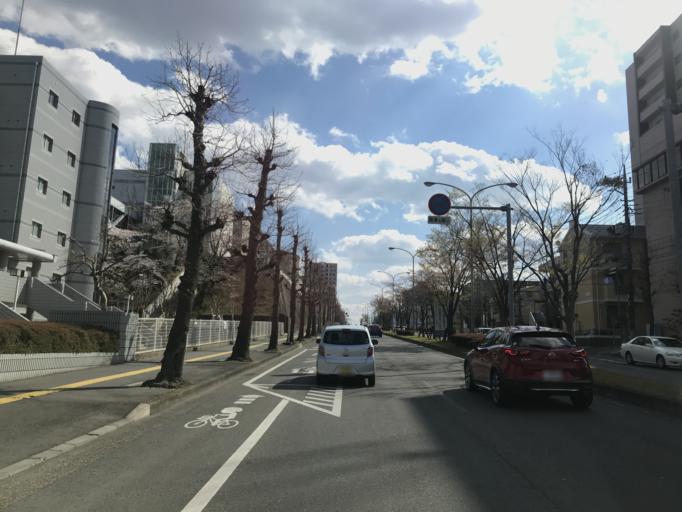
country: JP
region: Ibaraki
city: Mito-shi
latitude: 36.3645
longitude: 140.4751
